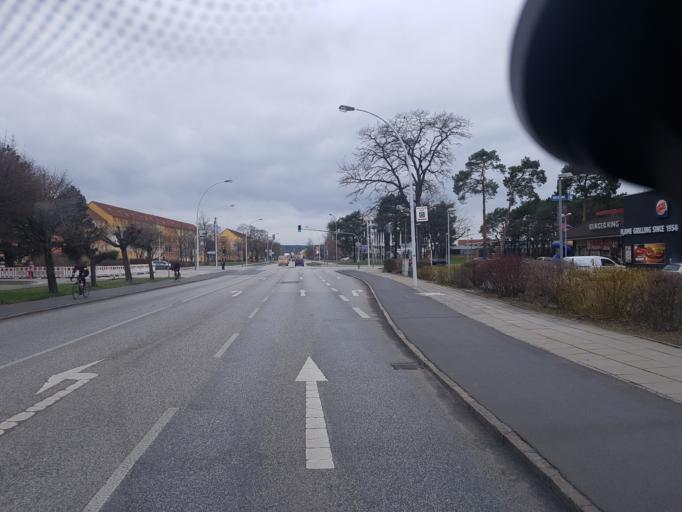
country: DE
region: Brandenburg
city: Eisenhuettenstadt
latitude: 52.1514
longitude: 14.6342
